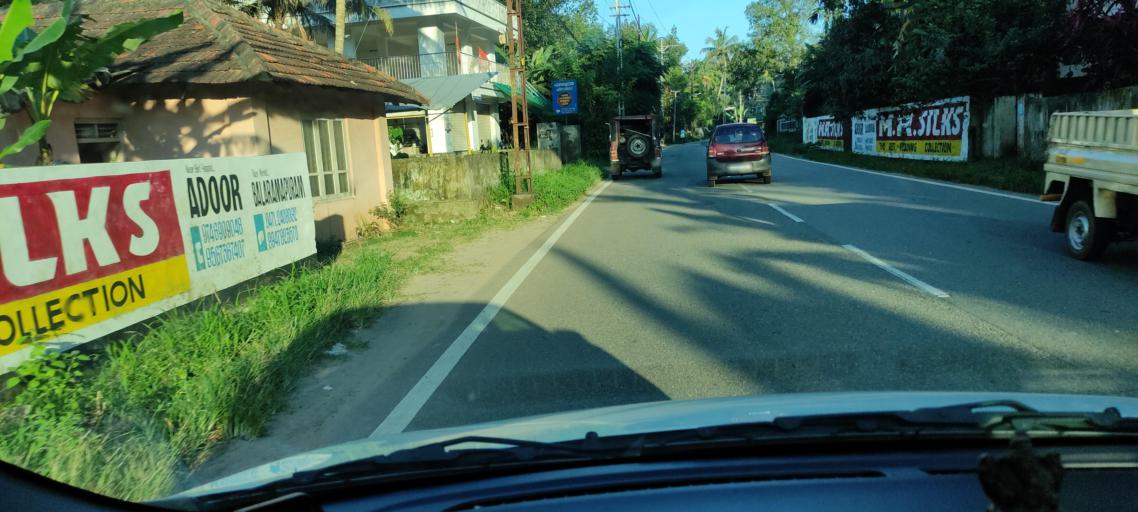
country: IN
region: Kerala
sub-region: Pattanamtitta
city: Adur
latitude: 9.1450
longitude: 76.7716
